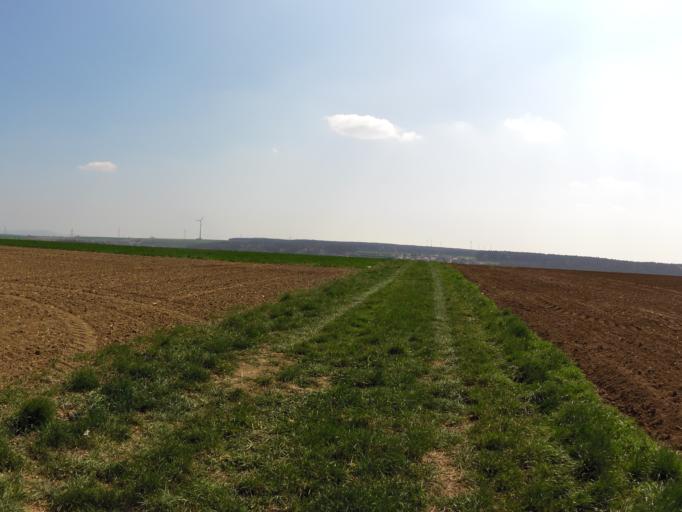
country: DE
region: Bavaria
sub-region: Regierungsbezirk Unterfranken
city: Theilheim
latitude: 49.7612
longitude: 10.0144
